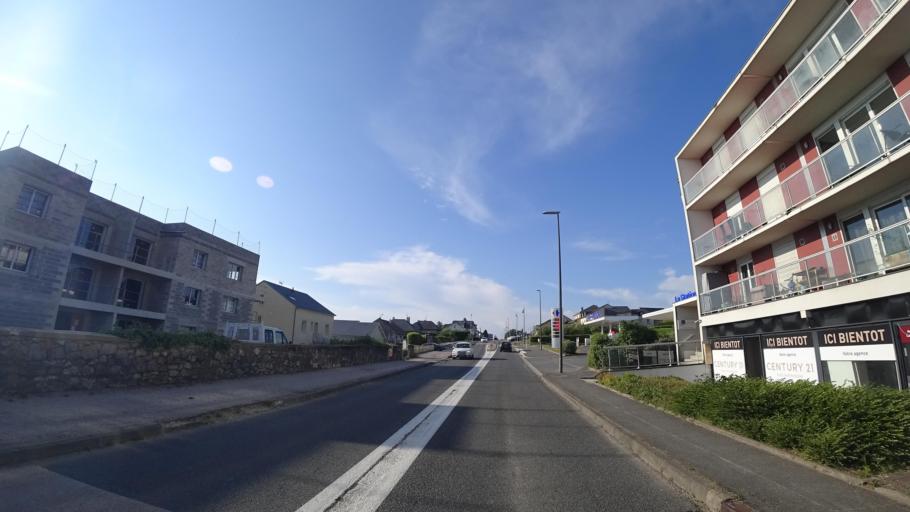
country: FR
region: Midi-Pyrenees
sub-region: Departement de l'Aveyron
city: Luc-la-Primaube
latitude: 44.2983
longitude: 2.5574
